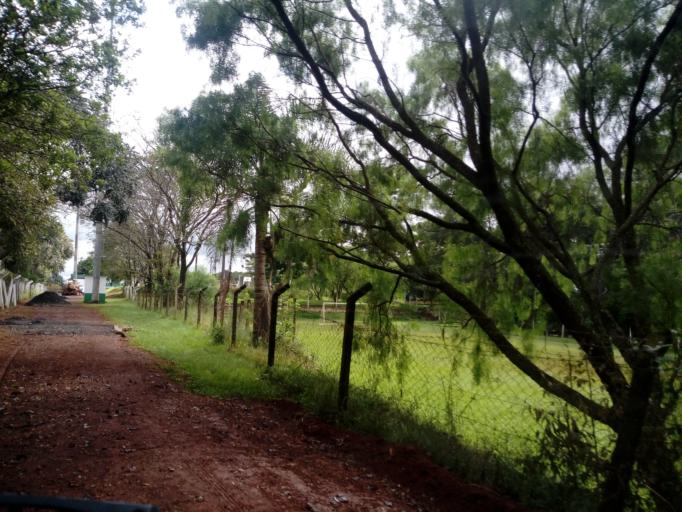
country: BR
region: Santa Catarina
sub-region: Chapeco
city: Chapeco
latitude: -27.0999
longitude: -52.6433
